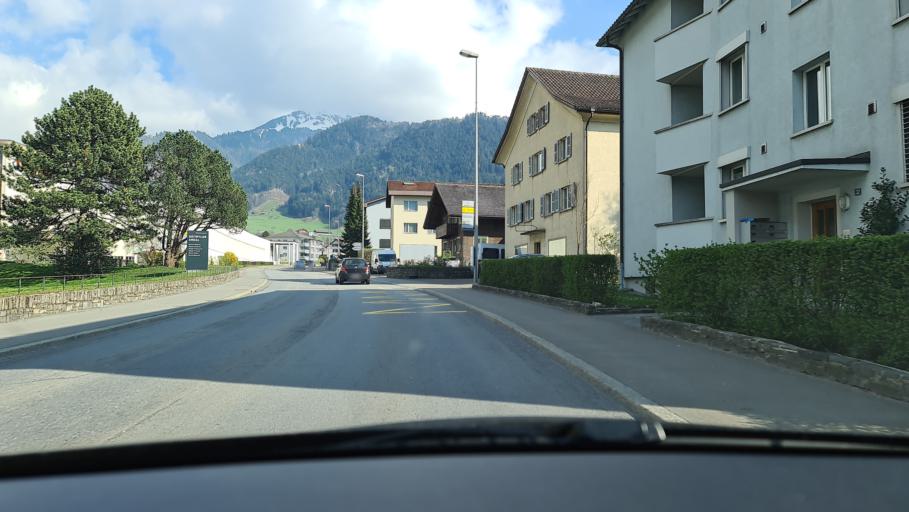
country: CH
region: Uri
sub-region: Uri
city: Altdorf
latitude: 46.8776
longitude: 8.6460
